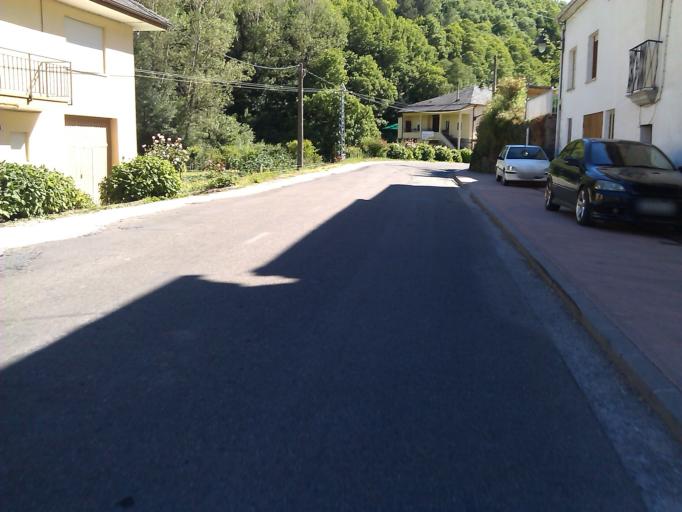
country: ES
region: Castille and Leon
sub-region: Provincia de Leon
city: Vega de Valcarce
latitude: 42.6646
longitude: -6.9406
